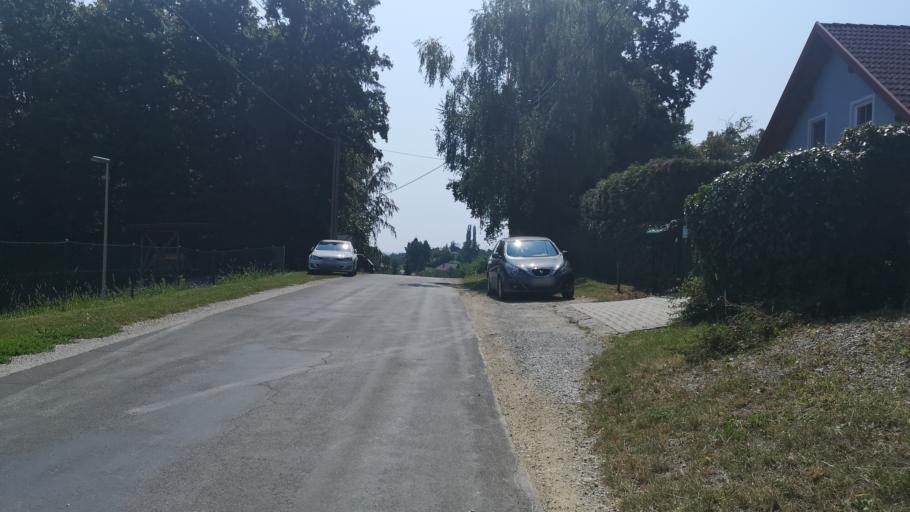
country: AT
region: Styria
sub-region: Politischer Bezirk Deutschlandsberg
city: Lannach
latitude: 46.9306
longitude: 15.3532
